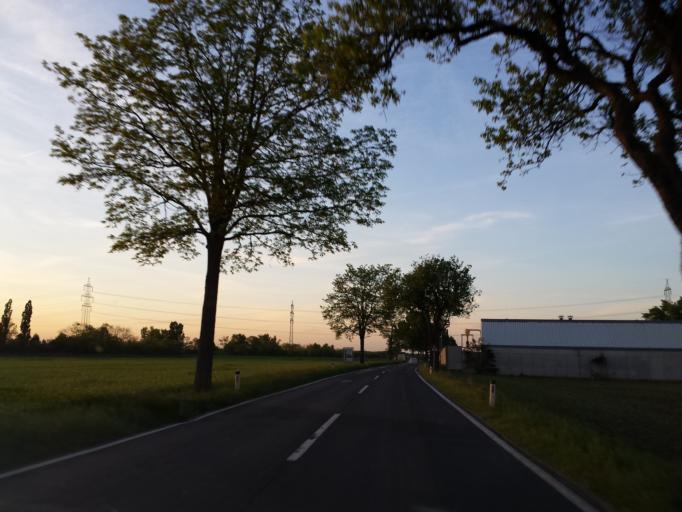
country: AT
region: Lower Austria
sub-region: Politischer Bezirk Tulln
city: Atzenbrugg
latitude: 48.3292
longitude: 15.9084
